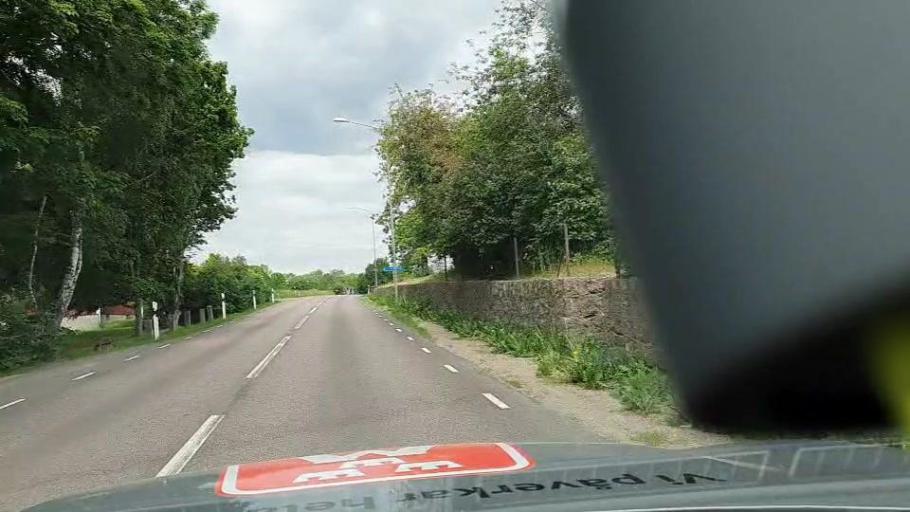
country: SE
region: Blekinge
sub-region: Karlskrona Kommun
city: Rodeby
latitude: 56.4290
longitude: 15.5367
